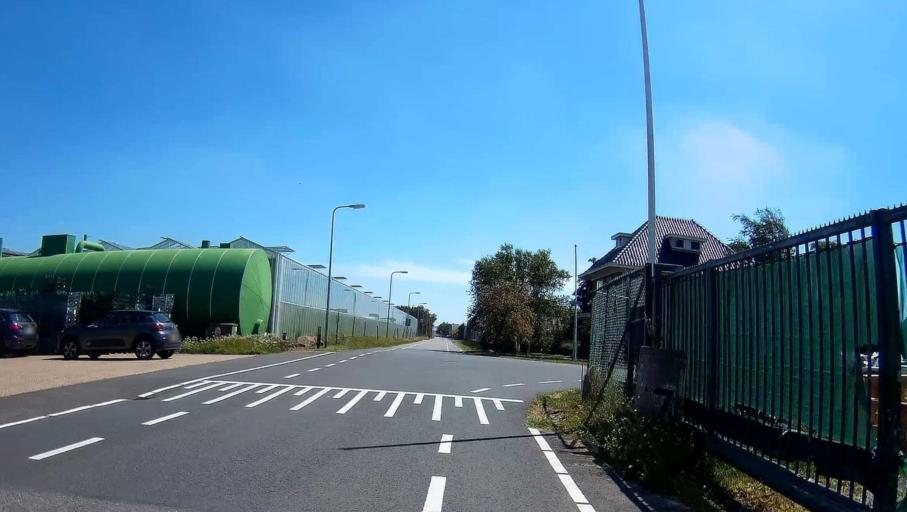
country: NL
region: South Holland
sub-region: Gemeente Westland
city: Monster
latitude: 52.0160
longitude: 4.1763
